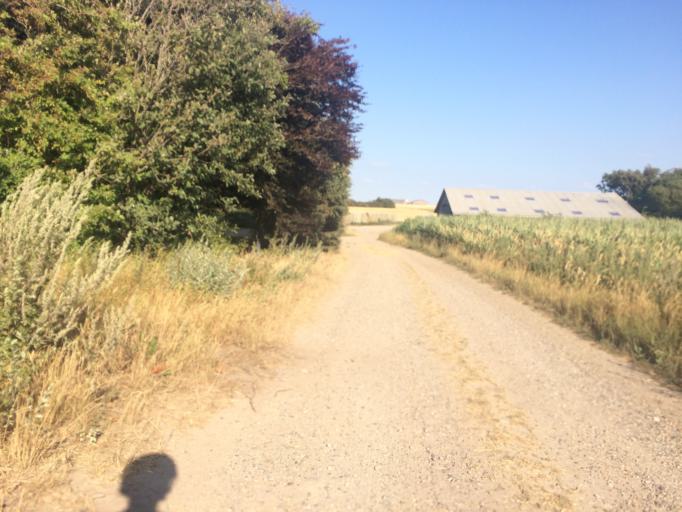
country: DK
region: Central Jutland
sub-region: Holstebro Kommune
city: Vinderup
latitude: 56.5902
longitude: 8.7403
